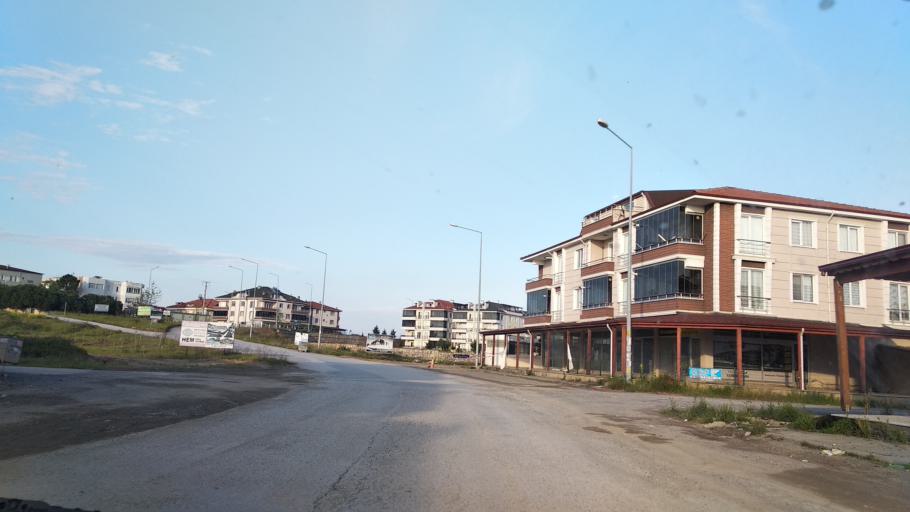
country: TR
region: Sakarya
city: Karasu
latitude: 41.0977
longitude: 30.7161
